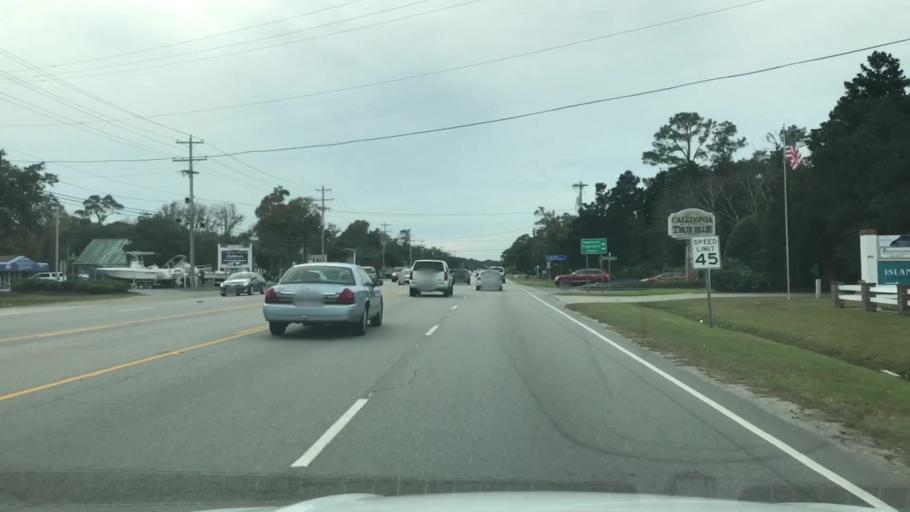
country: US
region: South Carolina
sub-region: Georgetown County
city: Murrells Inlet
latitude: 33.4341
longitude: -79.1370
